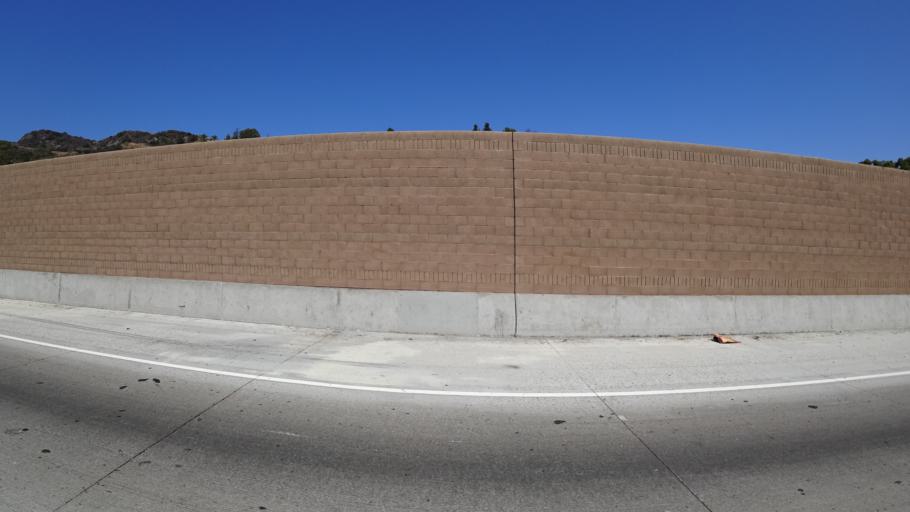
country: US
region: California
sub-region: Los Angeles County
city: Westwood, Los Angeles
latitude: 34.0868
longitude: -118.4748
